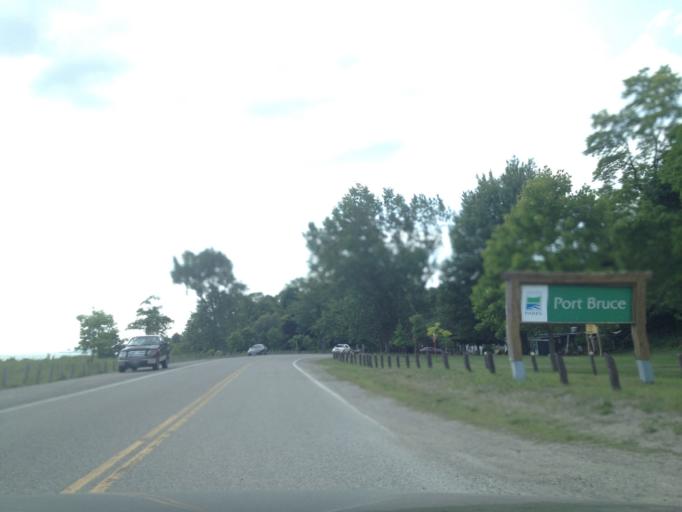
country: CA
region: Ontario
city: Aylmer
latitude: 42.6552
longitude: -81.0133
